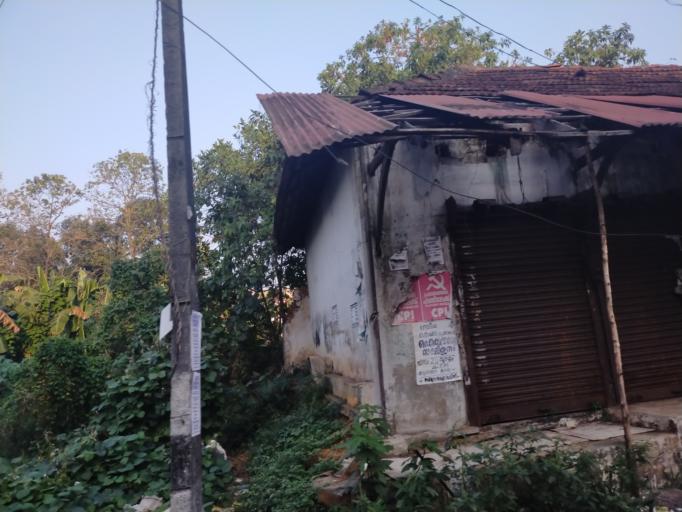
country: IN
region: Kerala
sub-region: Kottayam
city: Palackattumala
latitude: 9.7399
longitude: 76.5164
